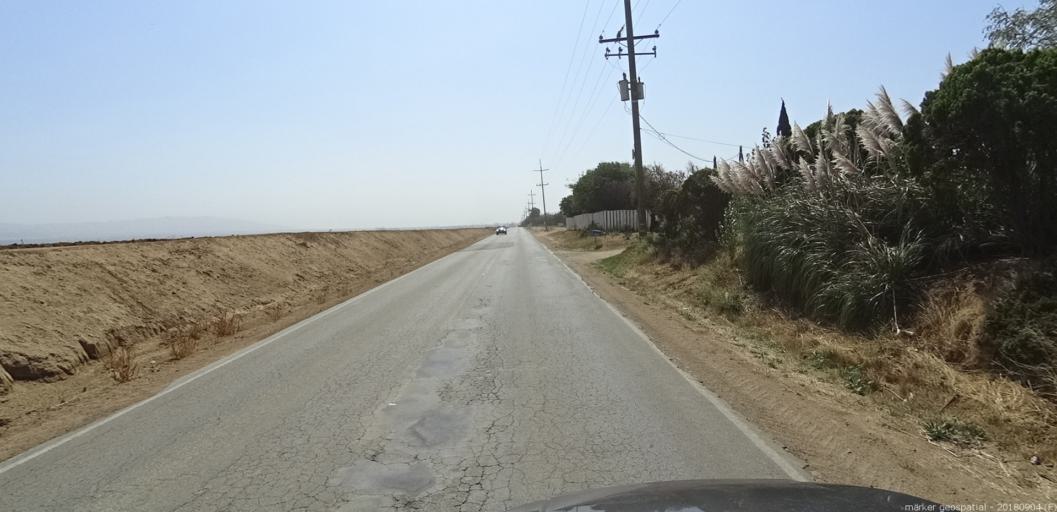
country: US
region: California
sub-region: Monterey County
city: Chualar
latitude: 36.5528
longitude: -121.4751
